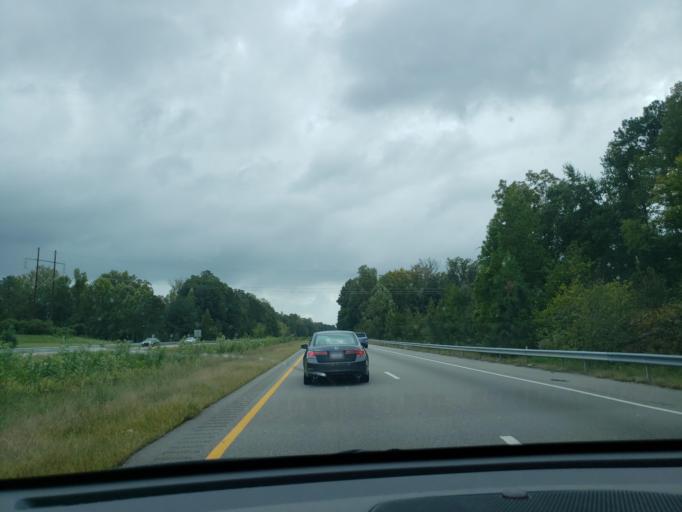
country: US
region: Virginia
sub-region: Mecklenburg County
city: Bracey
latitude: 36.5539
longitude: -78.1815
